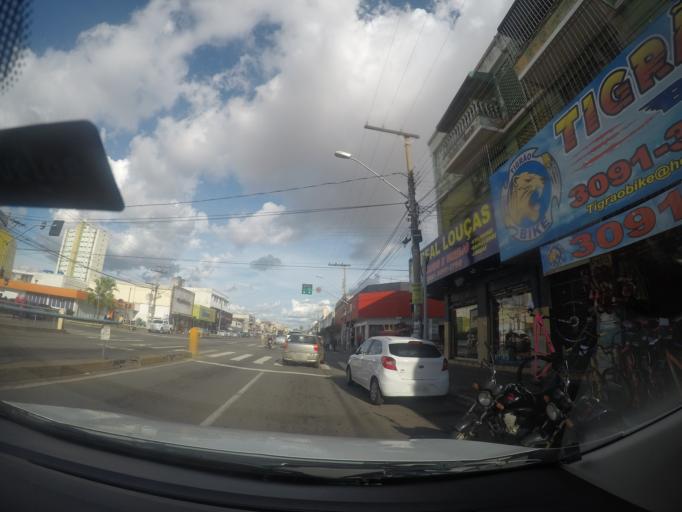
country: BR
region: Goias
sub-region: Goiania
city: Goiania
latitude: -16.6715
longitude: -49.2933
